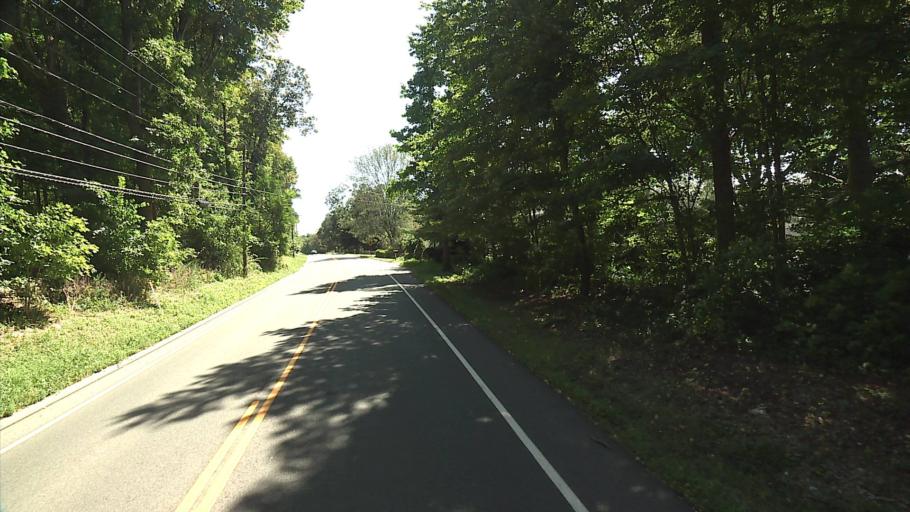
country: US
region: Connecticut
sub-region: New Haven County
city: Oxford
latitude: 41.4118
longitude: -73.1464
